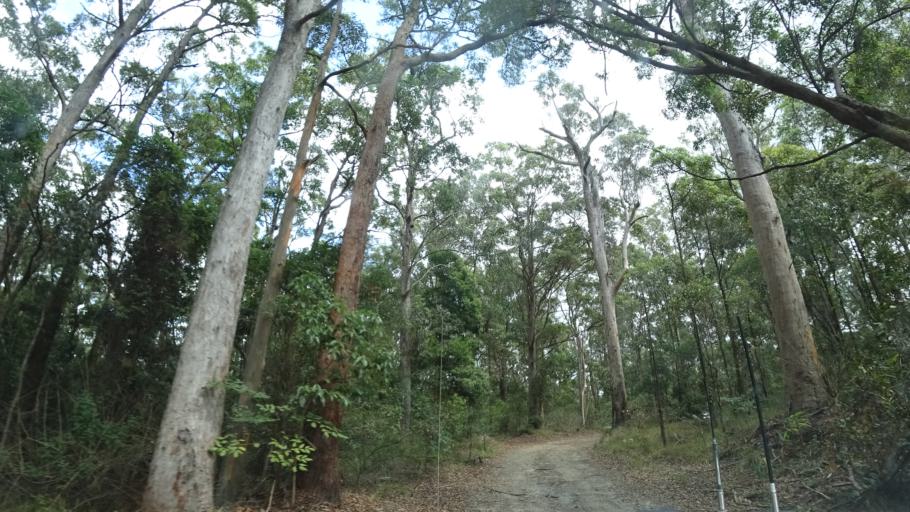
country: AU
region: Queensland
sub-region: Moreton Bay
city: Highvale
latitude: -27.4009
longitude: 152.8012
